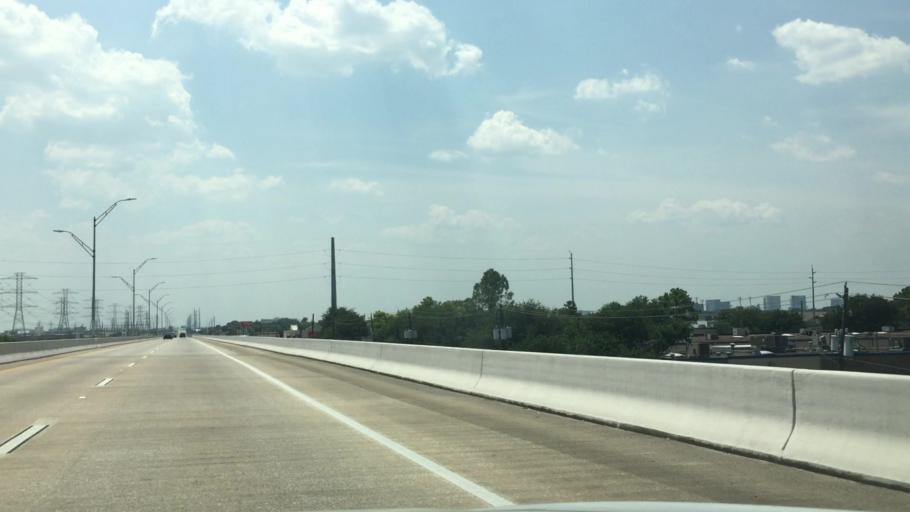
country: US
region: Texas
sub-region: Harris County
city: Piney Point Village
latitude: 29.7216
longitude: -95.5167
